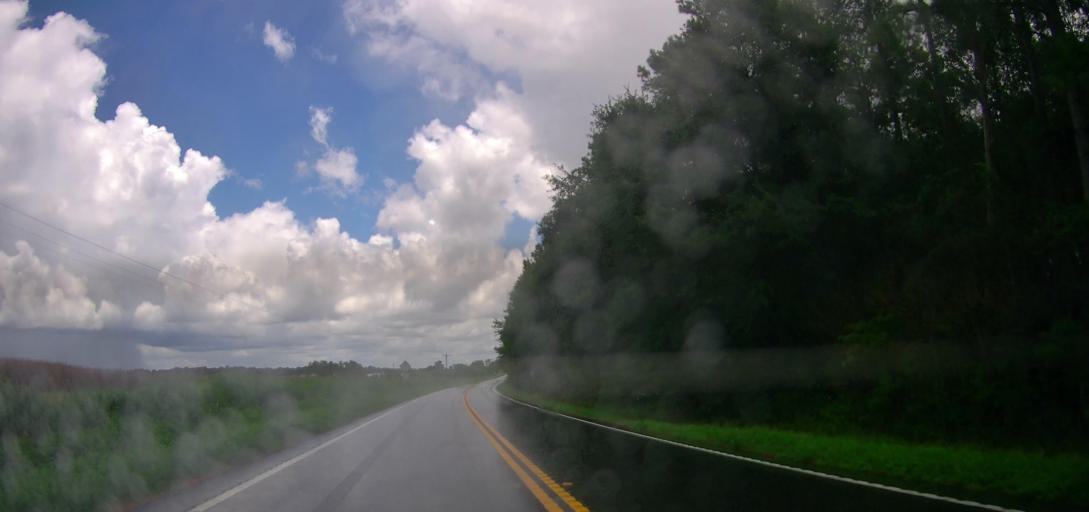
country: US
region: Georgia
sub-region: Pulaski County
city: Hawkinsville
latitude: 32.1796
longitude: -83.5342
